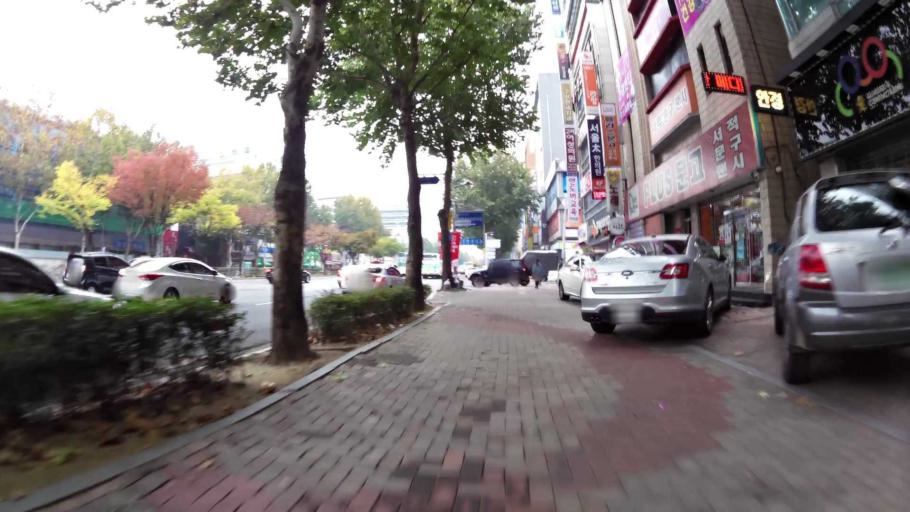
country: KR
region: Daegu
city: Daegu
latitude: 35.8586
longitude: 128.6337
